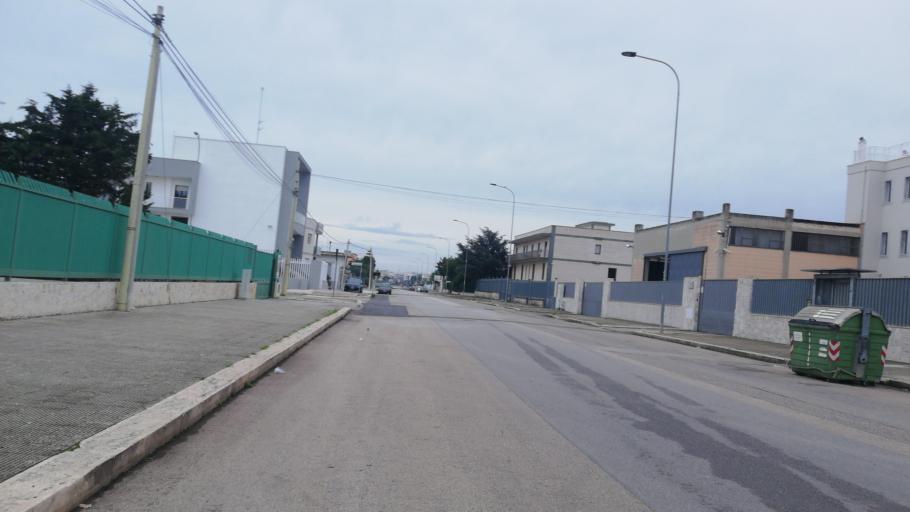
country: IT
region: Apulia
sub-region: Provincia di Bari
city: Bitonto
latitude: 41.1182
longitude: 16.6777
